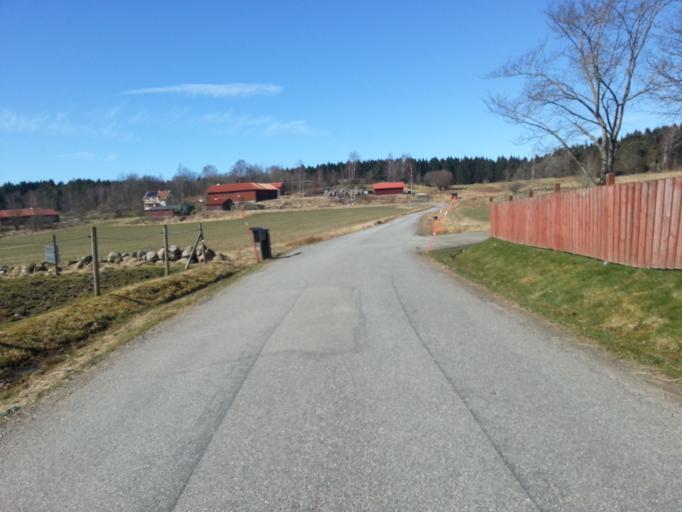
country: SE
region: Vaestra Goetaland
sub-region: Kungalvs Kommun
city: Kungalv
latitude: 57.9029
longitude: 11.9542
